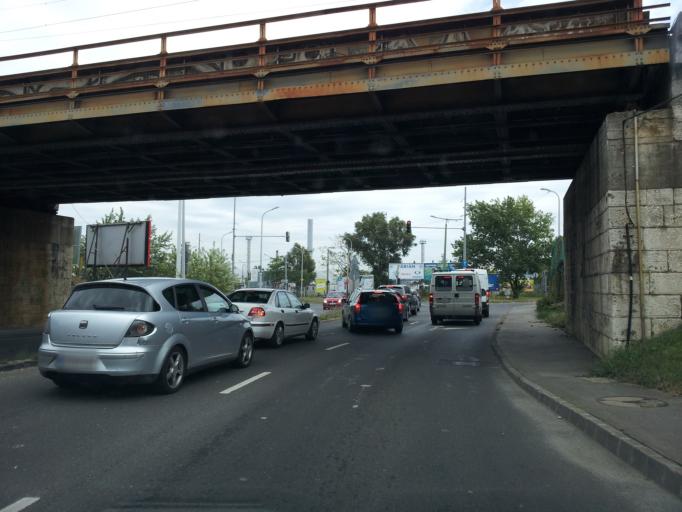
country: HU
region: Budapest
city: Budapest XI. keruelet
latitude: 47.4744
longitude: 19.0233
